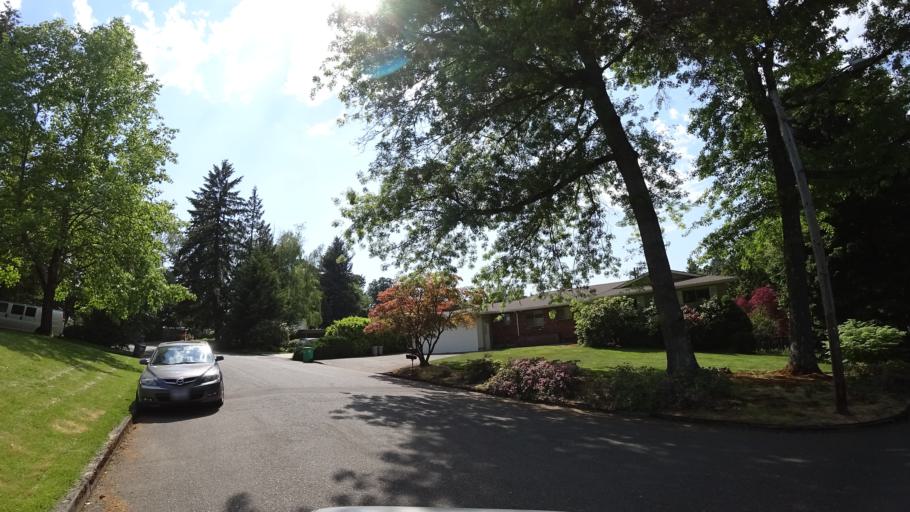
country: US
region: Oregon
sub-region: Washington County
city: Metzger
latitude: 45.4486
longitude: -122.7376
